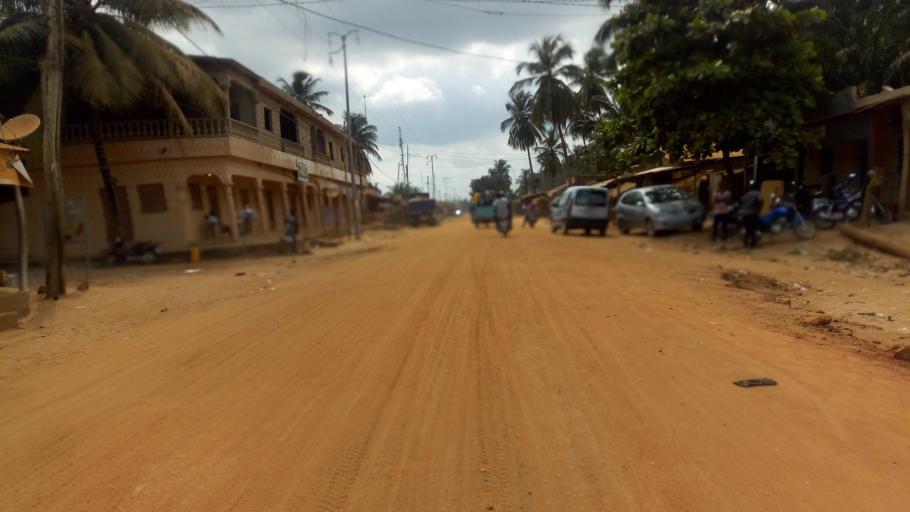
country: TG
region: Maritime
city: Tsevie
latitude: 6.3209
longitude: 1.2224
